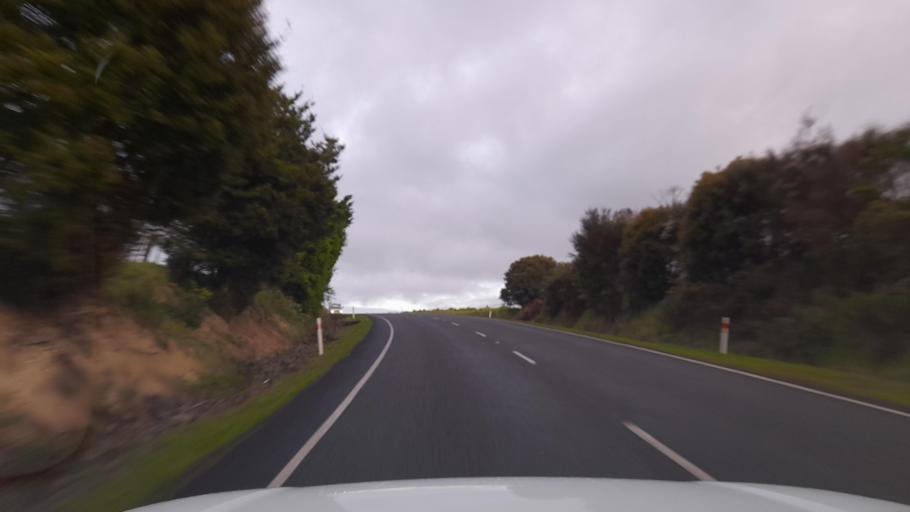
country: NZ
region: Northland
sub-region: Whangarei
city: Maungatapere
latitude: -35.7222
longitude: 174.0419
